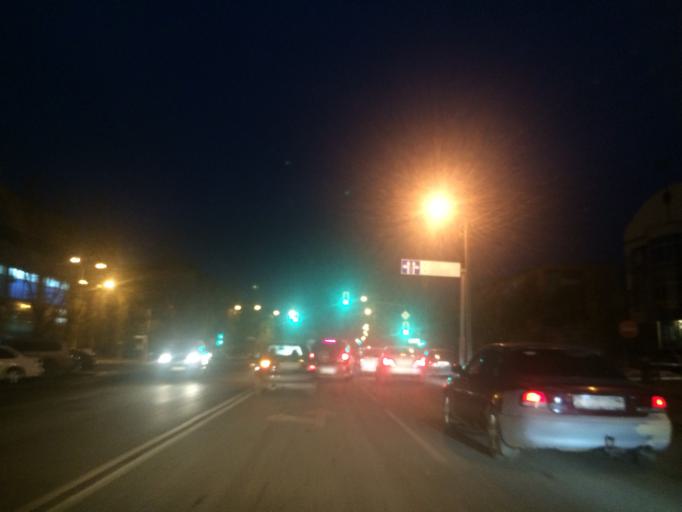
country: KZ
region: Astana Qalasy
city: Astana
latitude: 51.1859
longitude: 71.4215
